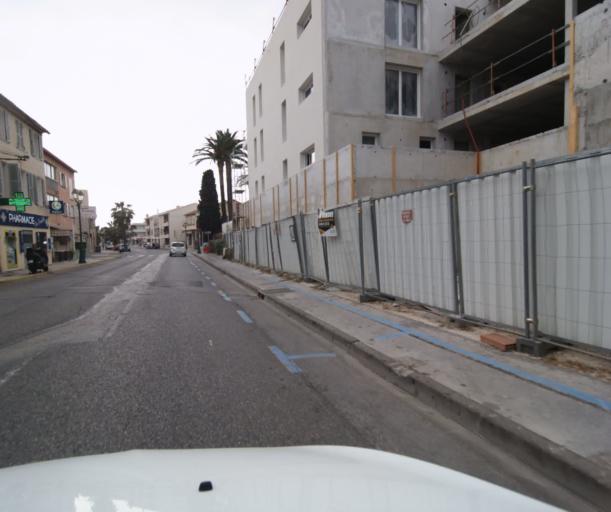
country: FR
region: Provence-Alpes-Cote d'Azur
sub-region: Departement du Var
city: Le Pradet
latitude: 43.1068
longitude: 6.0200
